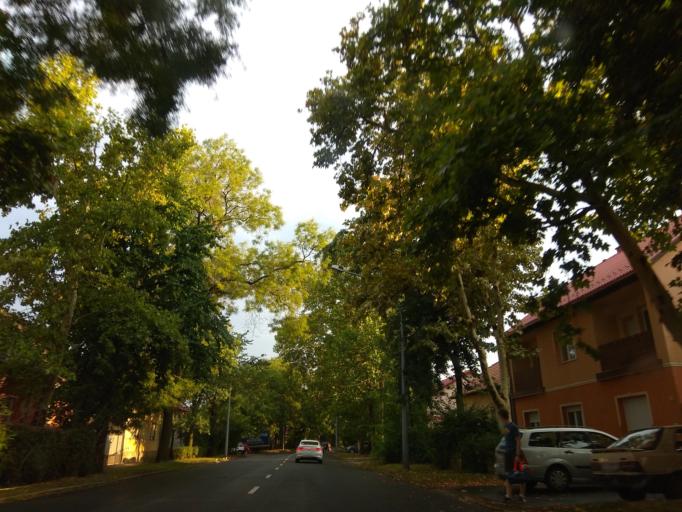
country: HU
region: Borsod-Abauj-Zemplen
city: Miskolc
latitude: 48.0923
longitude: 20.7957
